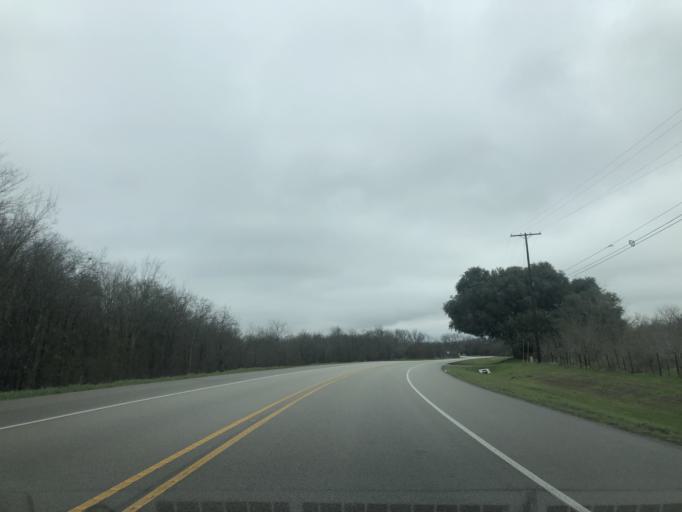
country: US
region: Texas
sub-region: Williamson County
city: Georgetown
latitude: 30.6461
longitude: -97.5798
